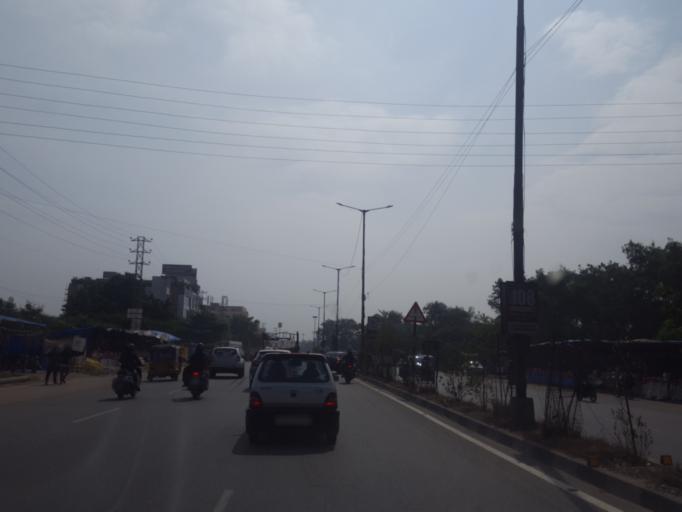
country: IN
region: Telangana
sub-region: Medak
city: Serilingampalle
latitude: 17.5005
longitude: 78.3129
